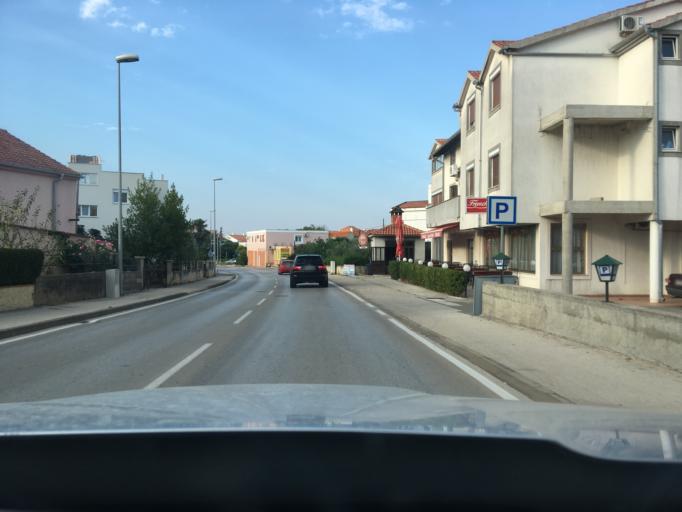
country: HR
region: Zadarska
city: Zadar
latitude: 44.1327
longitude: 15.2307
